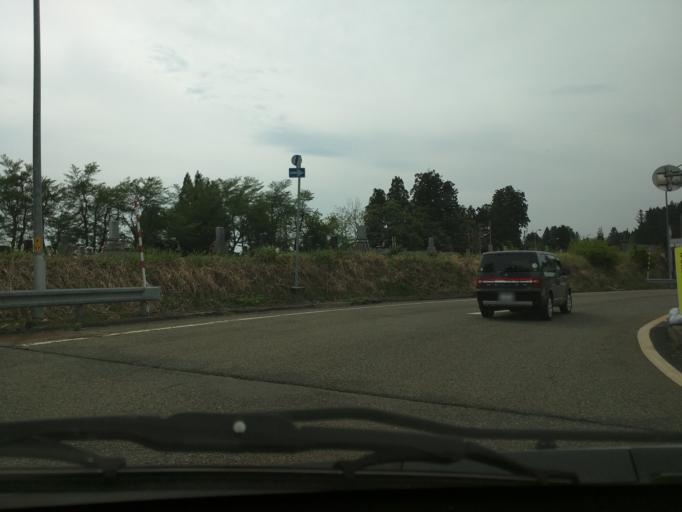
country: JP
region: Niigata
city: Ojiya
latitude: 37.2539
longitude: 138.9263
